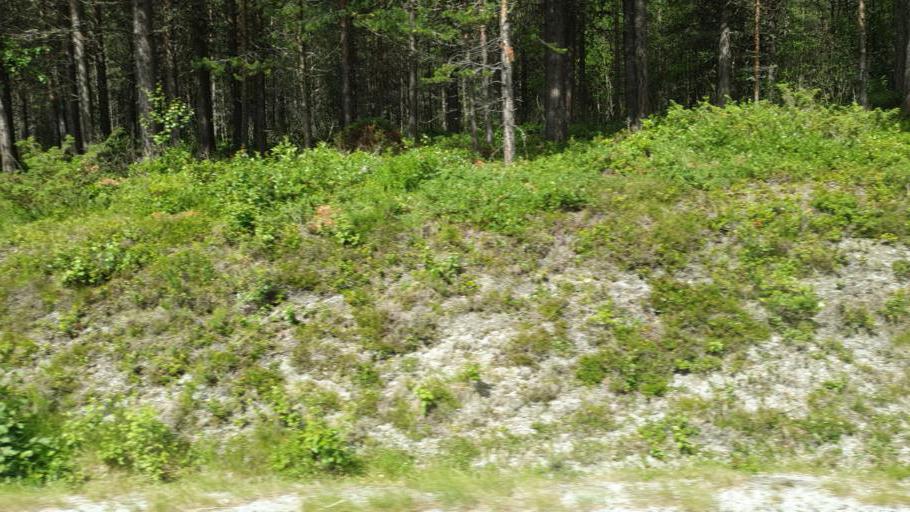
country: NO
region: Oppland
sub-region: Vaga
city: Vagamo
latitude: 61.7324
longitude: 9.0860
